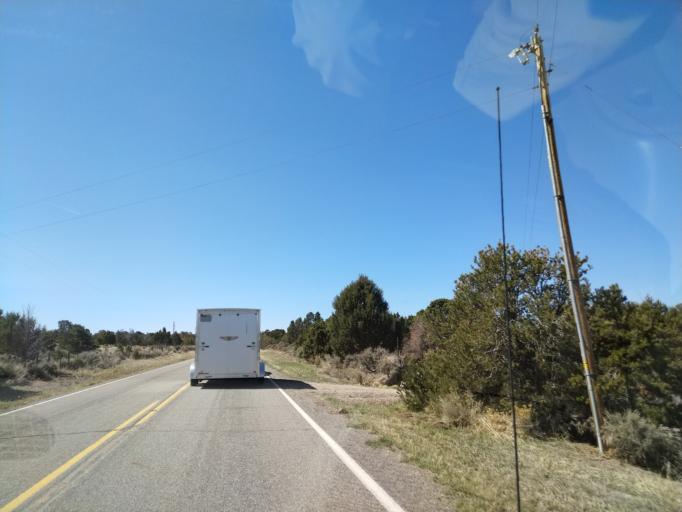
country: US
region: Colorado
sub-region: Mesa County
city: Redlands
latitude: 39.0011
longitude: -108.7099
